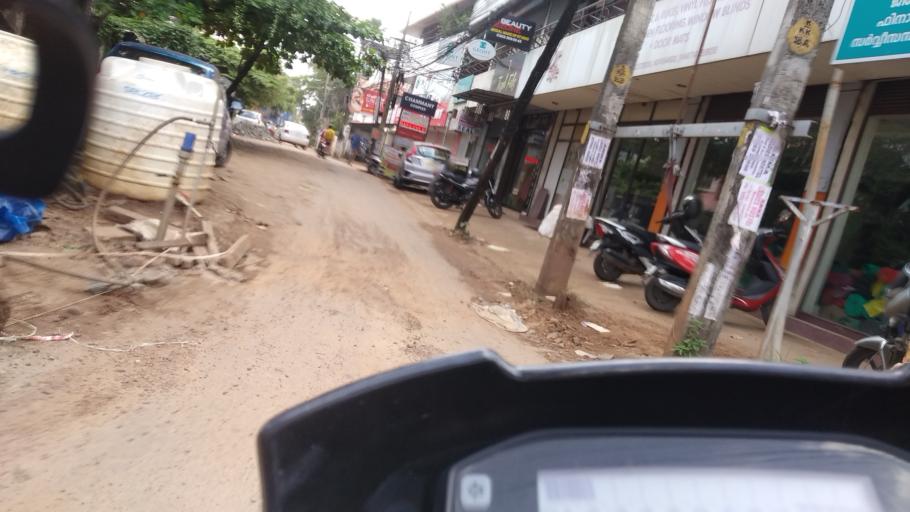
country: IN
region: Kerala
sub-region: Ernakulam
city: Cochin
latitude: 9.9914
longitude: 76.2931
